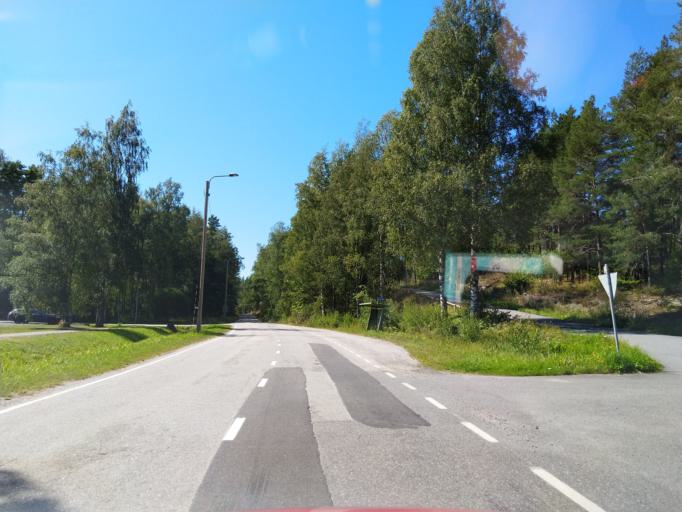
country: FI
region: Varsinais-Suomi
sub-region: Aboland-Turunmaa
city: Dragsfjaerd
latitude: 60.0188
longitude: 22.4833
